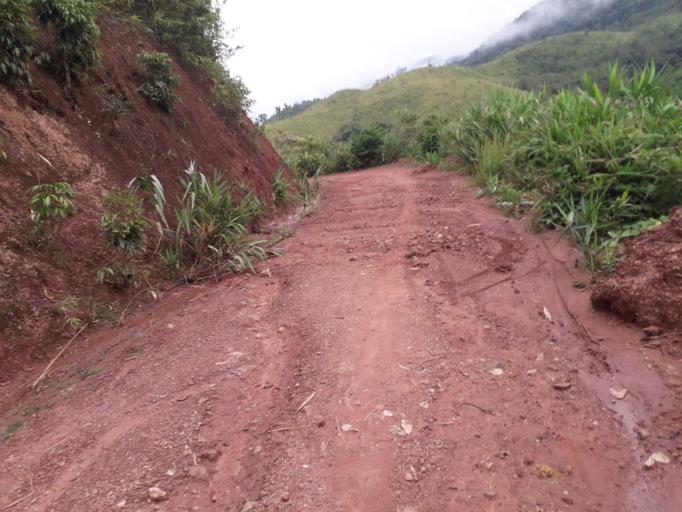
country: CN
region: Yunnan
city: Menglie
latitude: 22.2641
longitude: 101.5809
